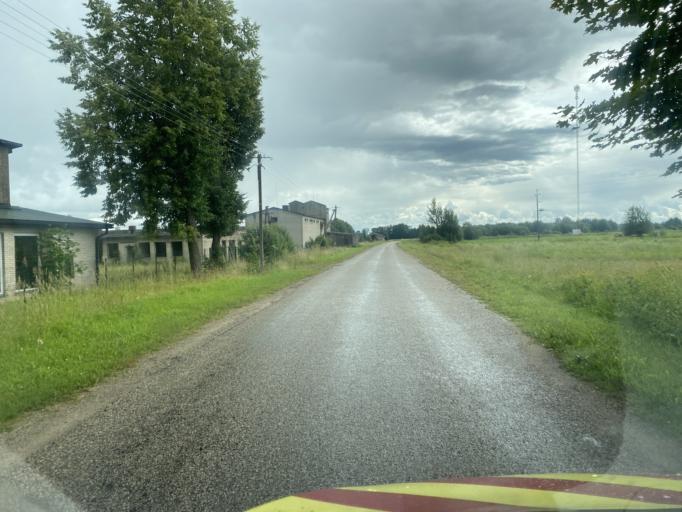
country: EE
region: Valgamaa
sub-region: Torva linn
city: Torva
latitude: 58.0948
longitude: 25.8979
